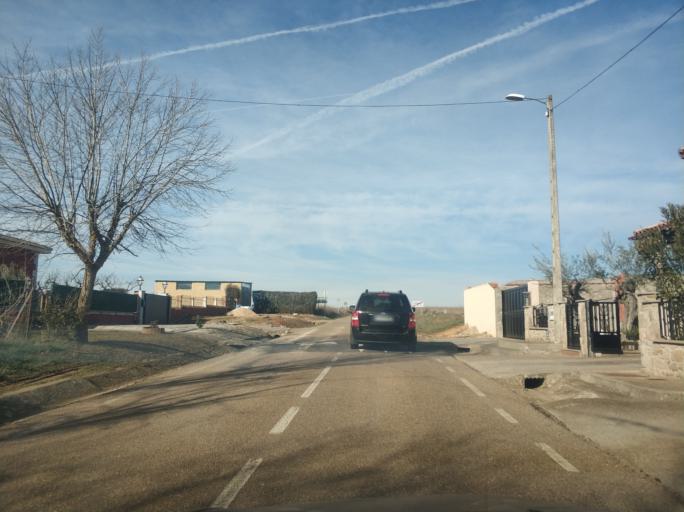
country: ES
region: Castille and Leon
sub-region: Provincia de Salamanca
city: Parada de Arriba
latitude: 40.9870
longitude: -5.7960
